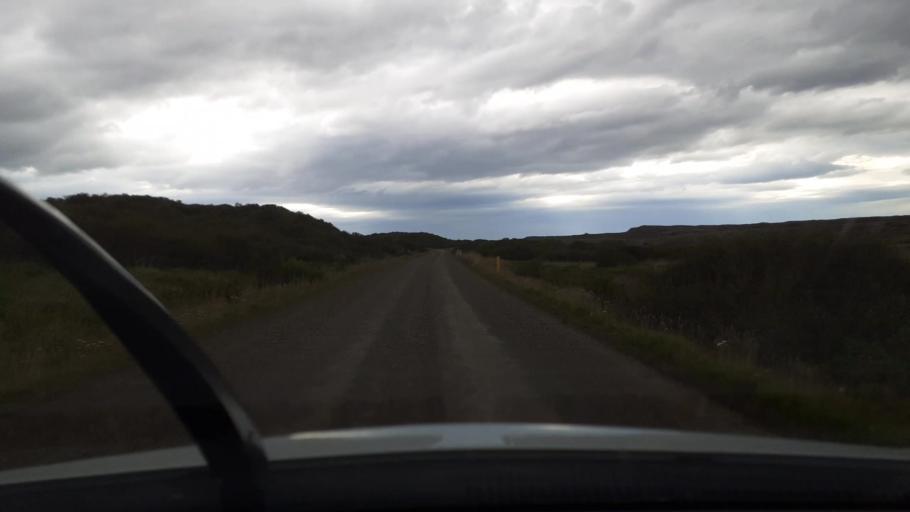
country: IS
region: West
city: Borgarnes
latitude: 64.6092
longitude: -21.9573
